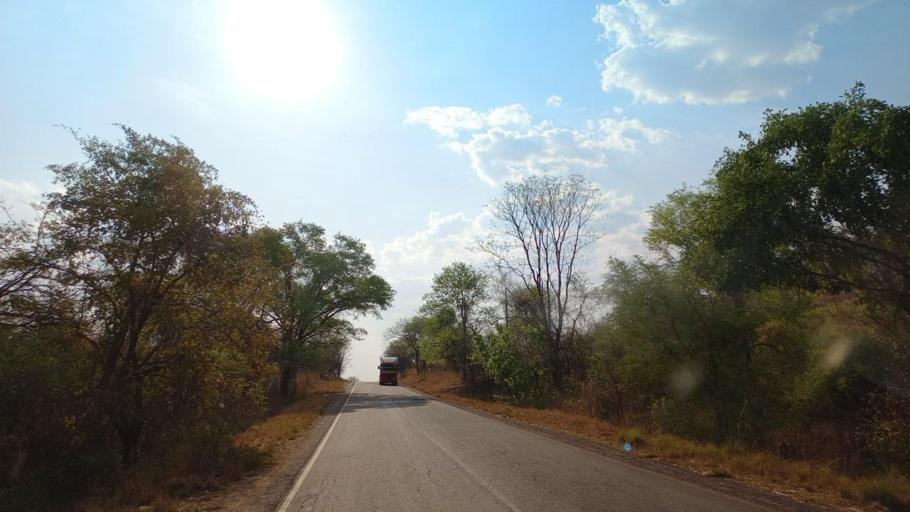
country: ZM
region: Lusaka
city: Luangwa
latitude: -14.9825
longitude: 30.1755
